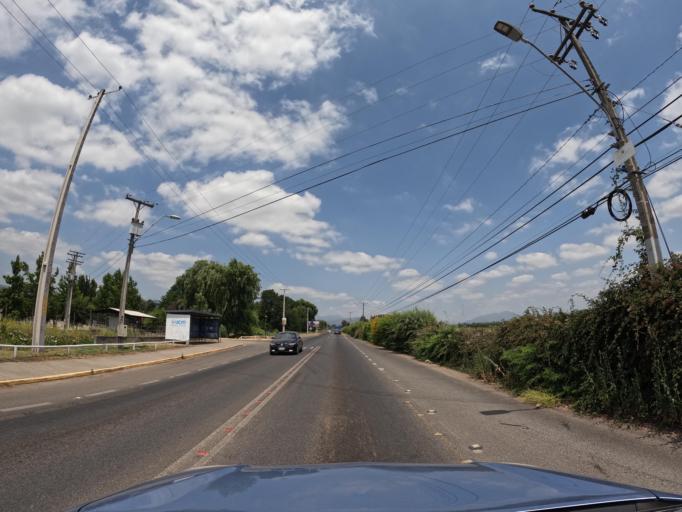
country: CL
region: Maule
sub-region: Provincia de Curico
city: Curico
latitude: -35.0282
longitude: -71.1951
